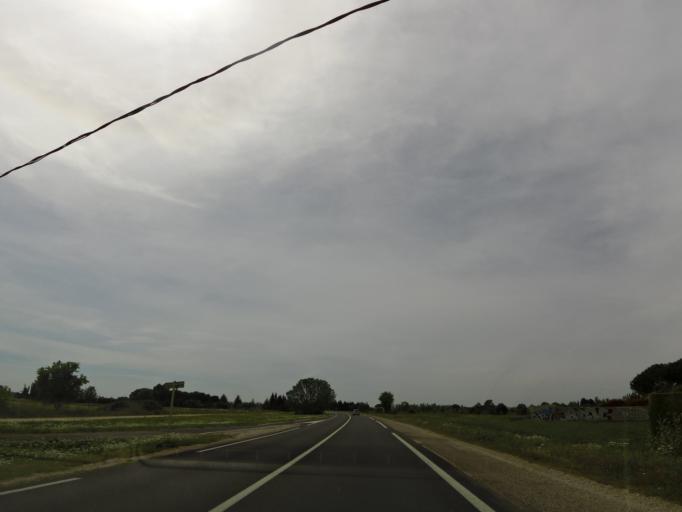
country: FR
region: Languedoc-Roussillon
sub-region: Departement de l'Herault
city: Lunel
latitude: 43.6668
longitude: 4.1411
